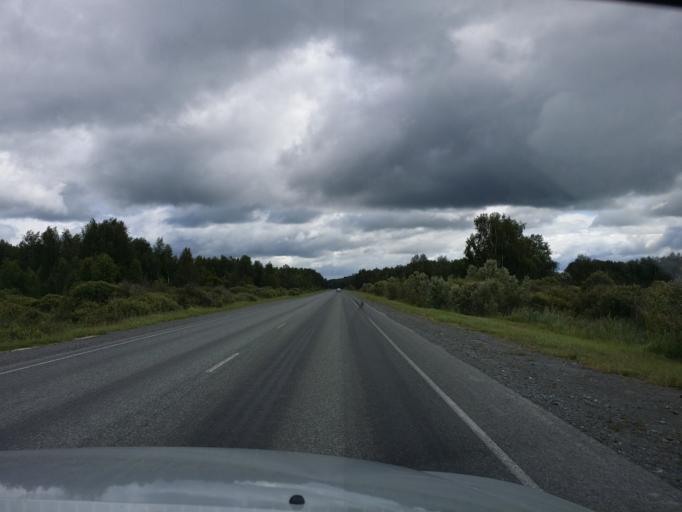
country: RU
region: Tjumen
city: Yarkovo
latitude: 57.5986
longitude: 67.2636
